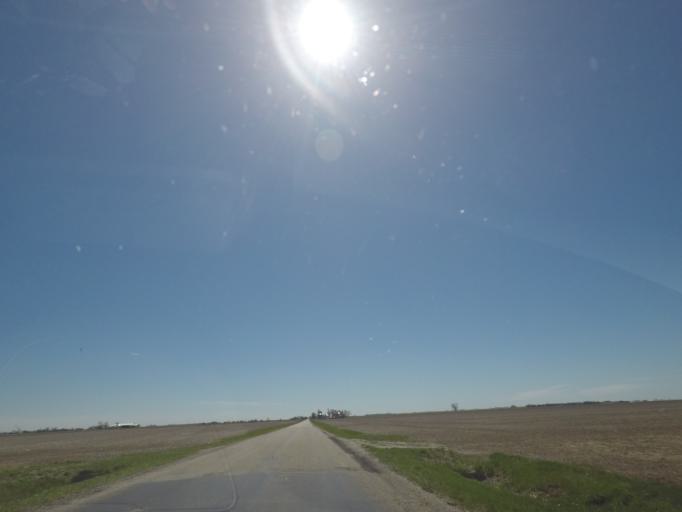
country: US
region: Illinois
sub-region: Logan County
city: Atlanta
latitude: 40.2082
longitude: -89.1944
